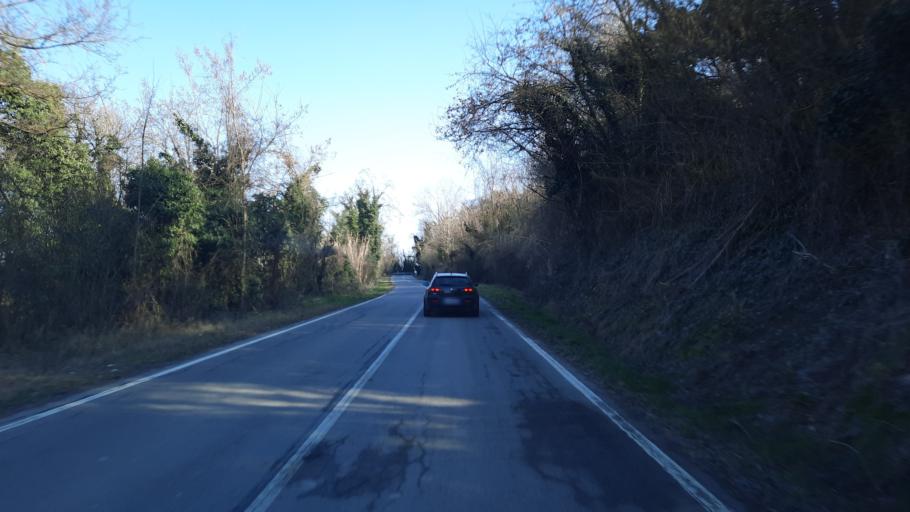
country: IT
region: Piedmont
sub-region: Provincia di Alessandria
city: Camino
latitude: 45.1664
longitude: 8.2879
